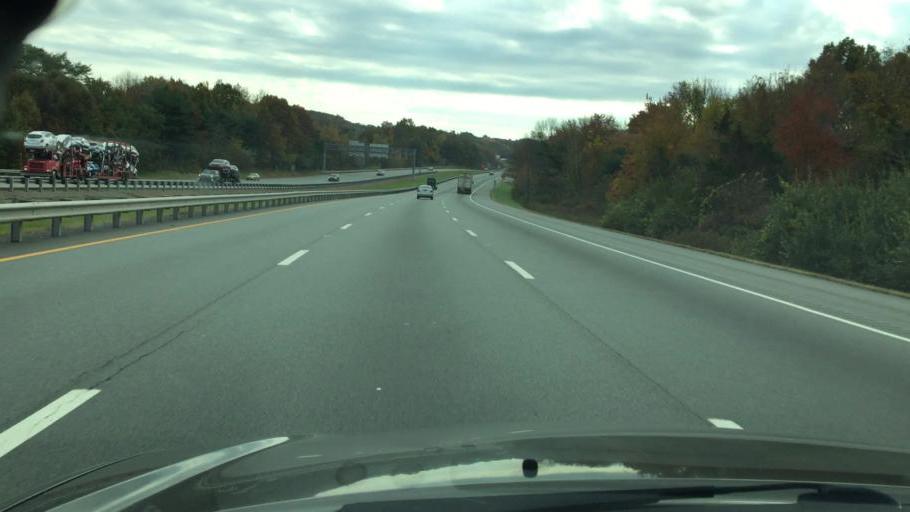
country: US
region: New Jersey
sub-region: Sussex County
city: Stanhope
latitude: 40.9032
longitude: -74.7219
